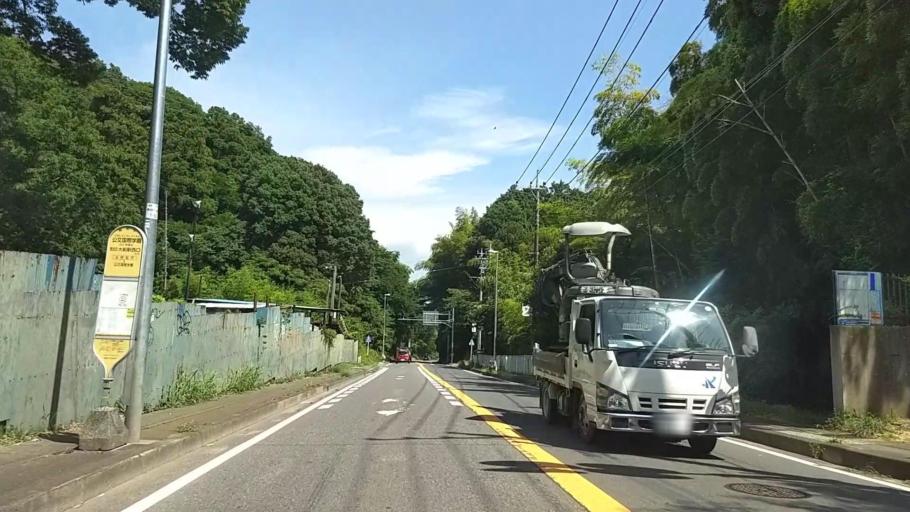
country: JP
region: Kanagawa
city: Fujisawa
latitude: 35.3719
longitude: 139.5141
